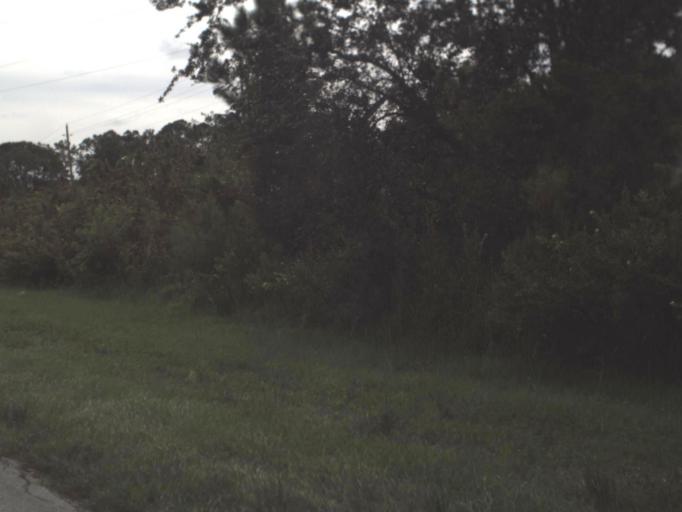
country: US
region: Florida
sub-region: Highlands County
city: Placid Lakes
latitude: 27.2112
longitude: -81.3487
